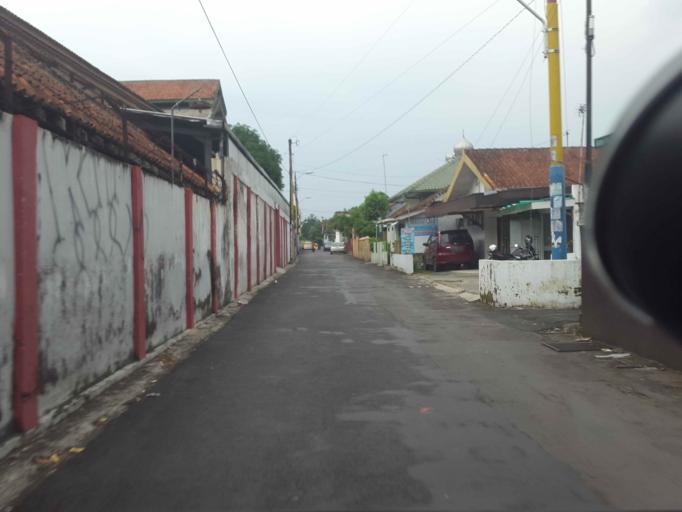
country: ID
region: Central Java
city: Purwokerto
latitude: -7.4223
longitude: 109.2408
